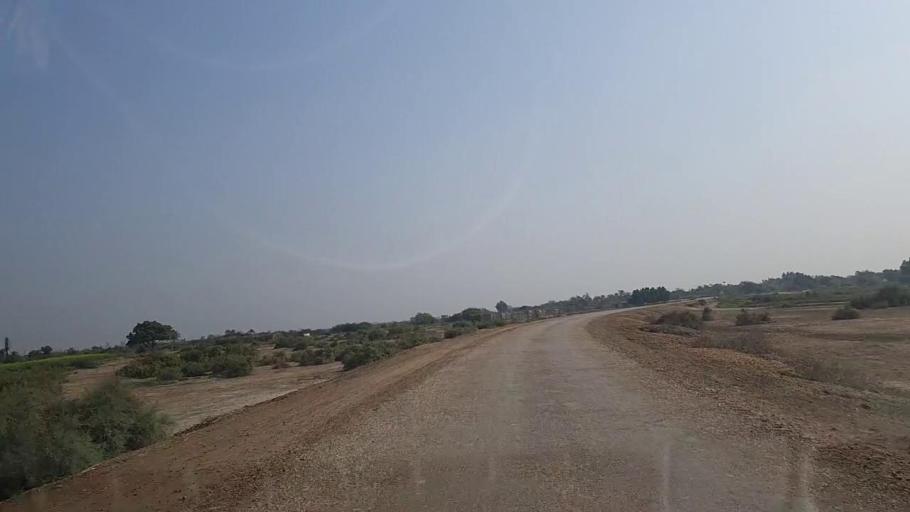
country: PK
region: Sindh
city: Keti Bandar
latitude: 24.2461
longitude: 67.6990
